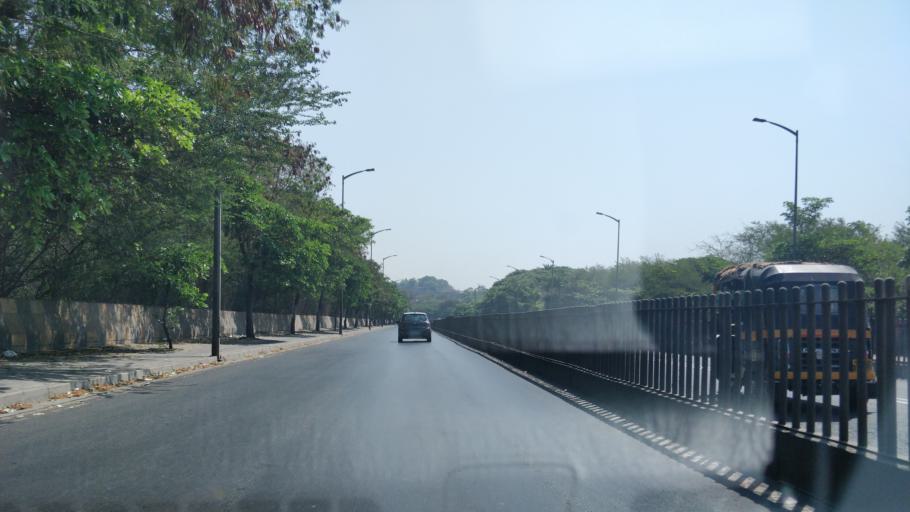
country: IN
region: Maharashtra
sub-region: Pune Division
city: Shivaji Nagar
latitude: 18.5421
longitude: 73.8726
